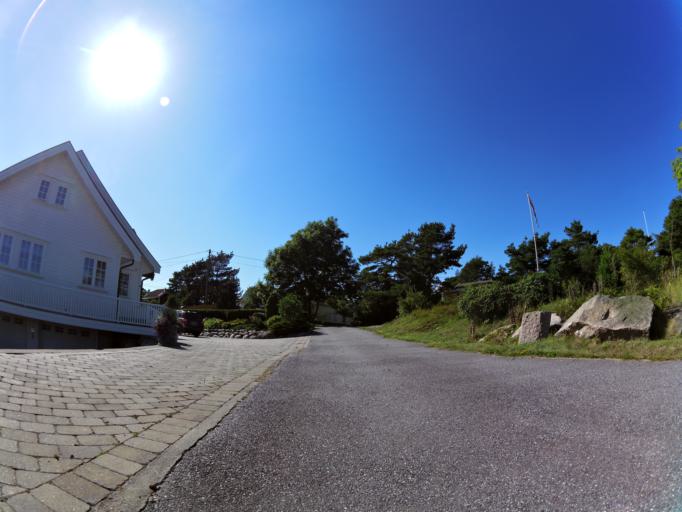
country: NO
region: Ostfold
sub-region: Fredrikstad
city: Fredrikstad
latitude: 59.1716
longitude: 10.8526
